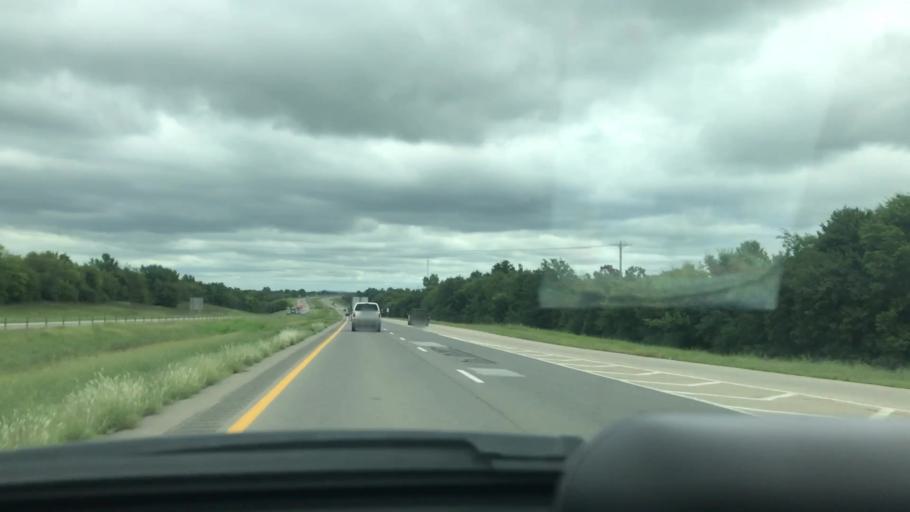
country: US
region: Oklahoma
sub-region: McIntosh County
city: Checotah
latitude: 35.4779
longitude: -95.5348
